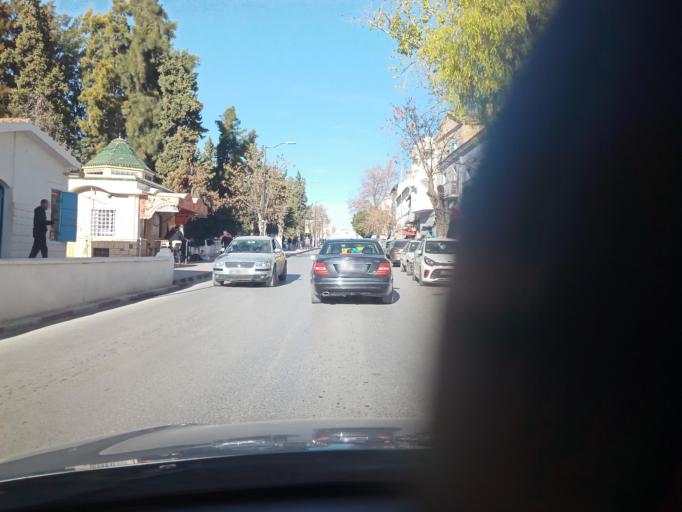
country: TN
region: Kef
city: El Kef
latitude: 36.1790
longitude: 8.7128
